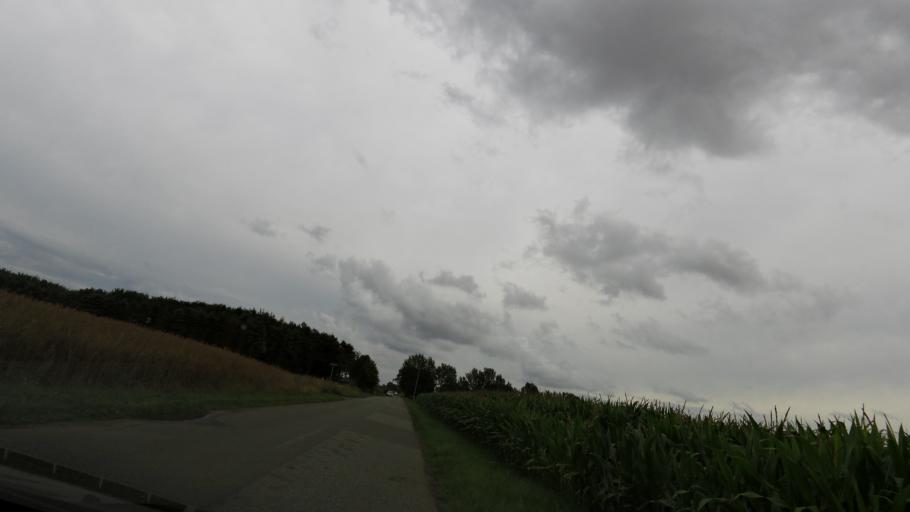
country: DK
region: South Denmark
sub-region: Nordfyns Kommune
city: Otterup
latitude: 55.5703
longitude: 10.4221
